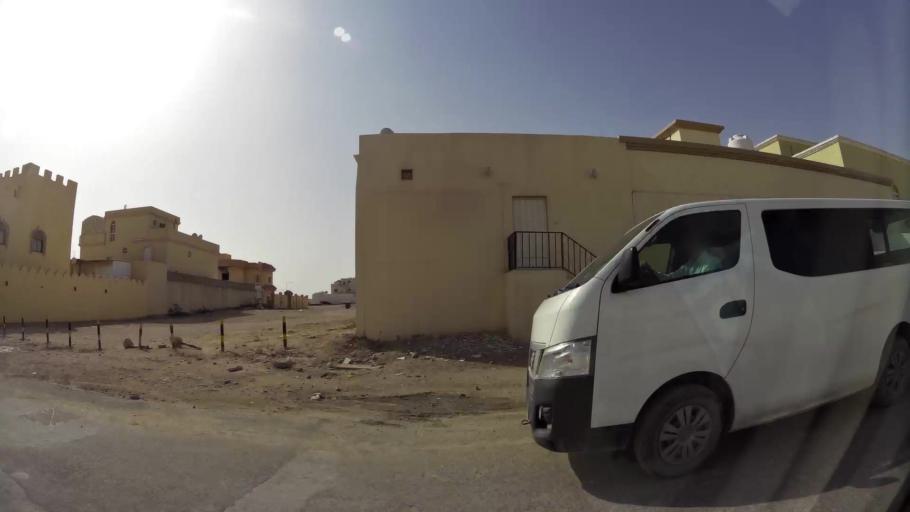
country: QA
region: Baladiyat ar Rayyan
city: Ar Rayyan
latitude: 25.3420
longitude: 51.4221
